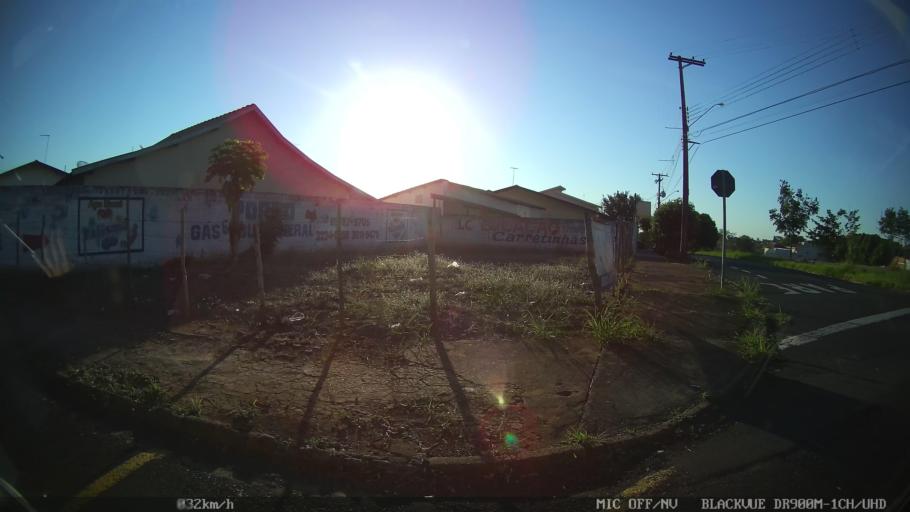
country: BR
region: Sao Paulo
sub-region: Sao Jose Do Rio Preto
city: Sao Jose do Rio Preto
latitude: -20.7903
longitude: -49.3627
